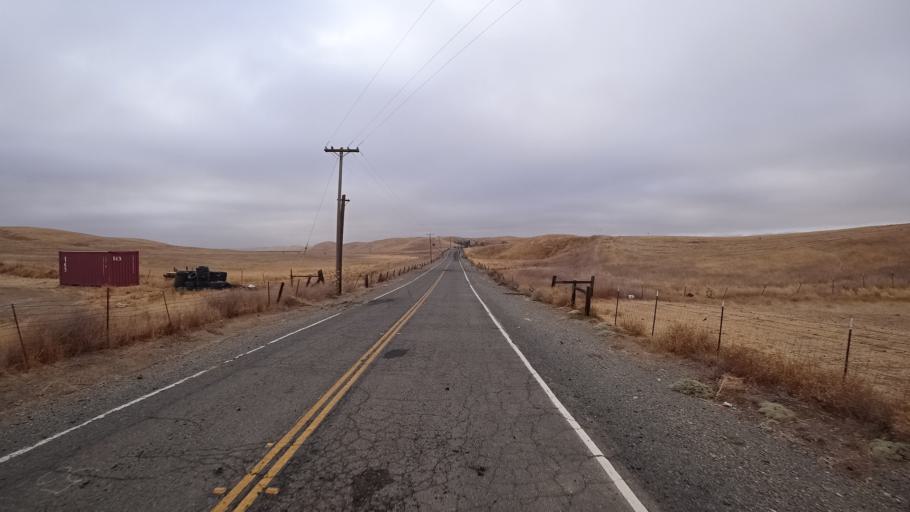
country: US
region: California
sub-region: Yolo County
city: Dunnigan
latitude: 38.8683
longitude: -122.0267
